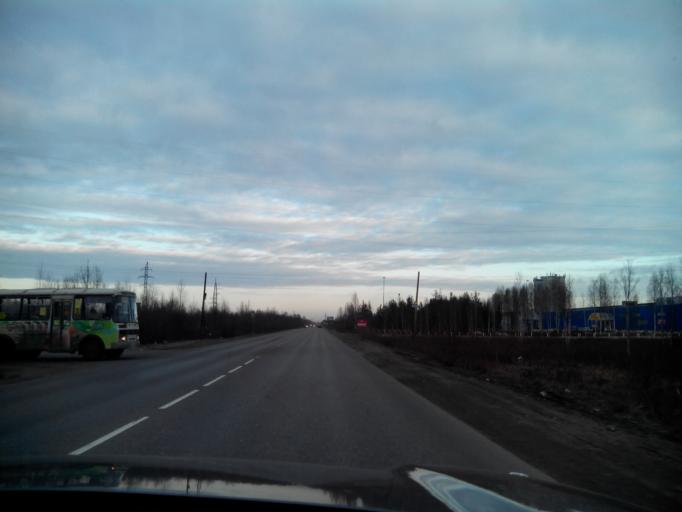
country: RU
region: Arkhangelskaya
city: Arkhangel'sk
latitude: 64.5307
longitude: 40.6517
